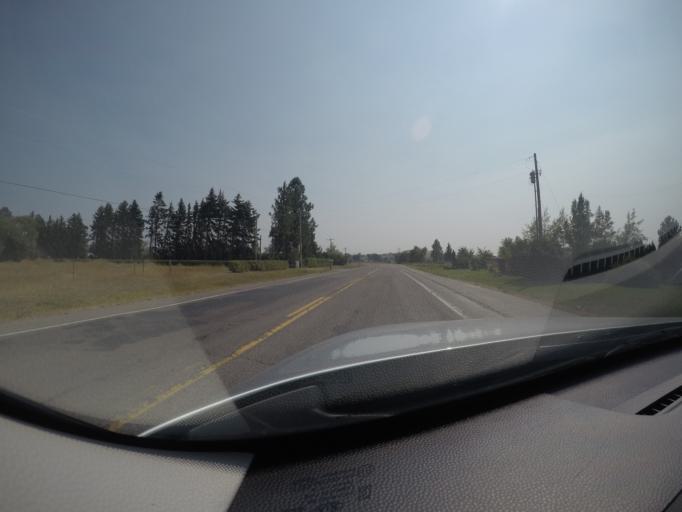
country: US
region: Montana
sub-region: Lake County
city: Polson
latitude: 47.7168
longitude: -114.1886
